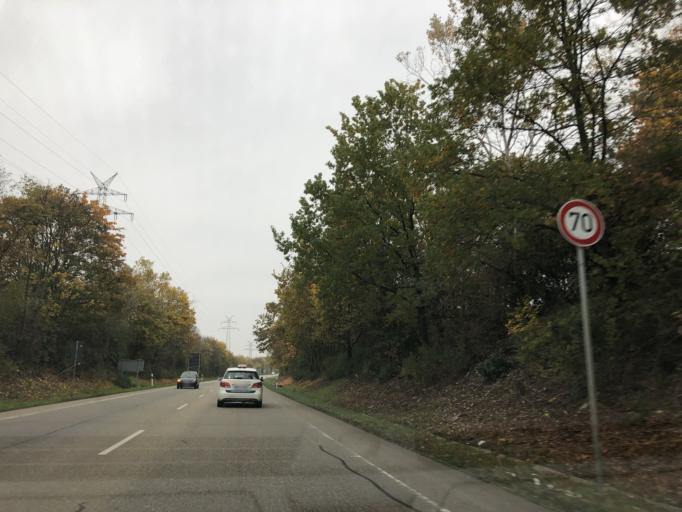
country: DE
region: Baden-Wuerttemberg
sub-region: Karlsruhe Region
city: Ilvesheim
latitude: 49.5009
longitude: 8.5342
